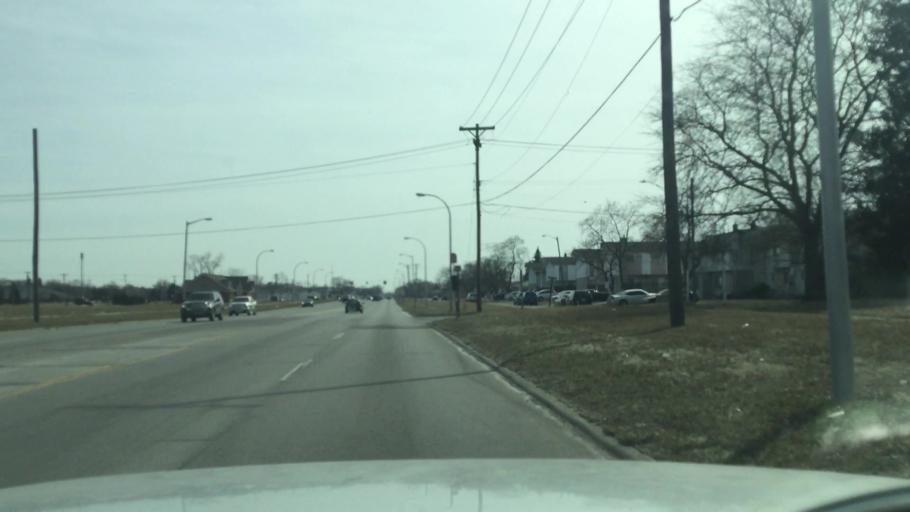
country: US
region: Michigan
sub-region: Wayne County
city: Inkster
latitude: 42.2852
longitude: -83.3292
